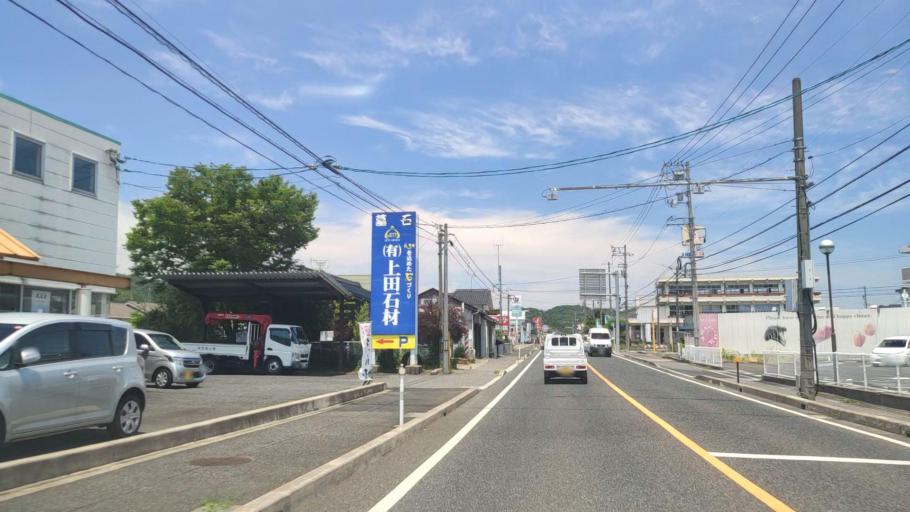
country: JP
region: Tottori
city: Tottori
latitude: 35.4138
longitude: 134.2552
